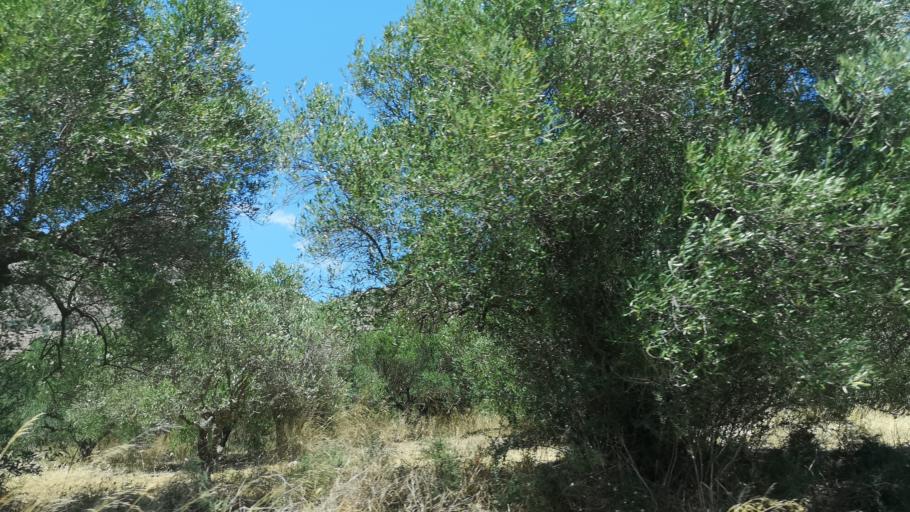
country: GR
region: Crete
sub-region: Nomos Lasithiou
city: Neapoli
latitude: 35.2464
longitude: 25.6313
